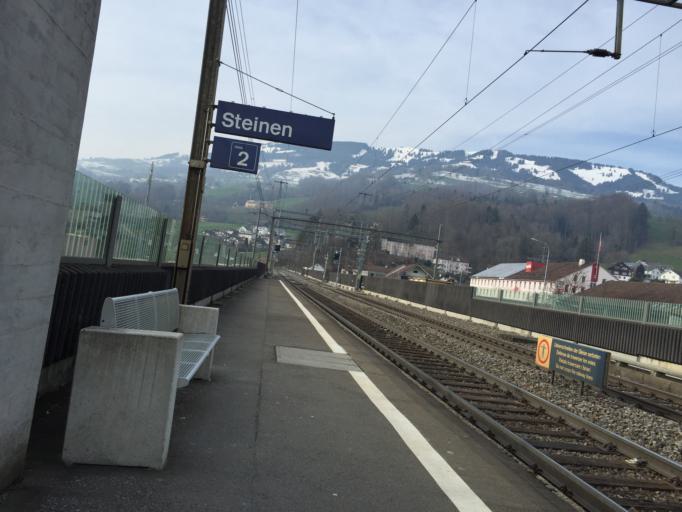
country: CH
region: Schwyz
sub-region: Bezirk Schwyz
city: Steinen
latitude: 47.0478
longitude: 8.6070
